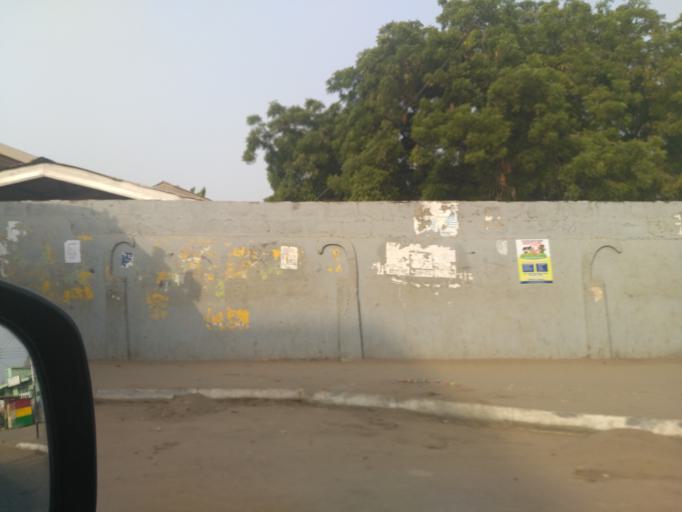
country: GH
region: Greater Accra
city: Accra
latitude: 5.5767
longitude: -0.2008
